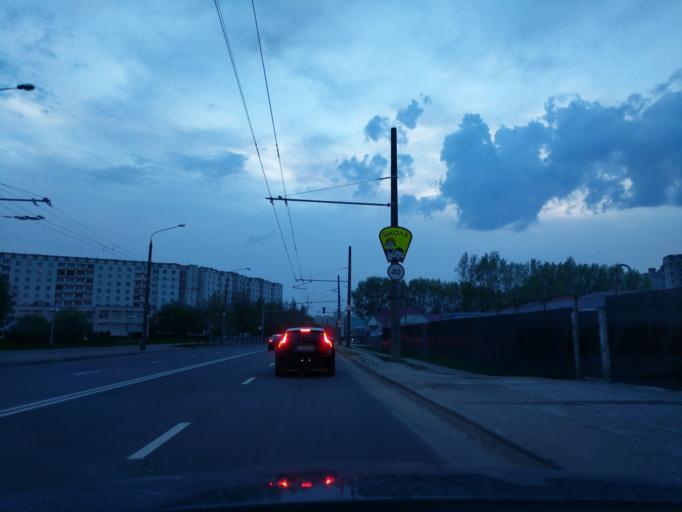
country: BY
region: Minsk
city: Novoye Medvezhino
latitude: 53.8722
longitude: 27.4712
